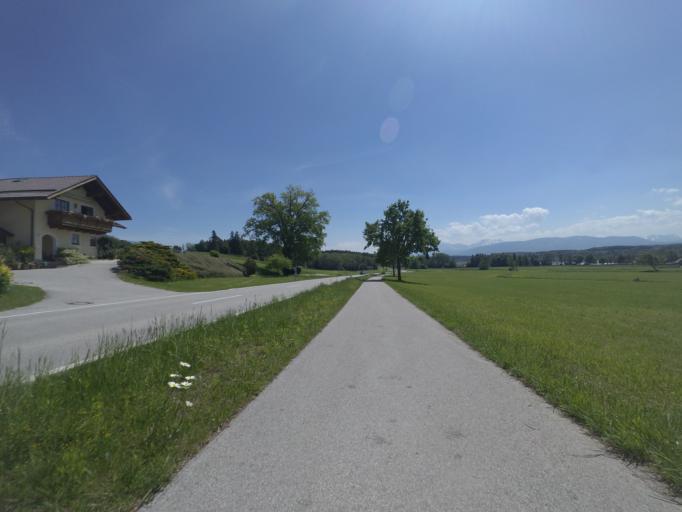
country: DE
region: Bavaria
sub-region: Upper Bavaria
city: Petting
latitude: 47.9333
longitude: 12.8053
